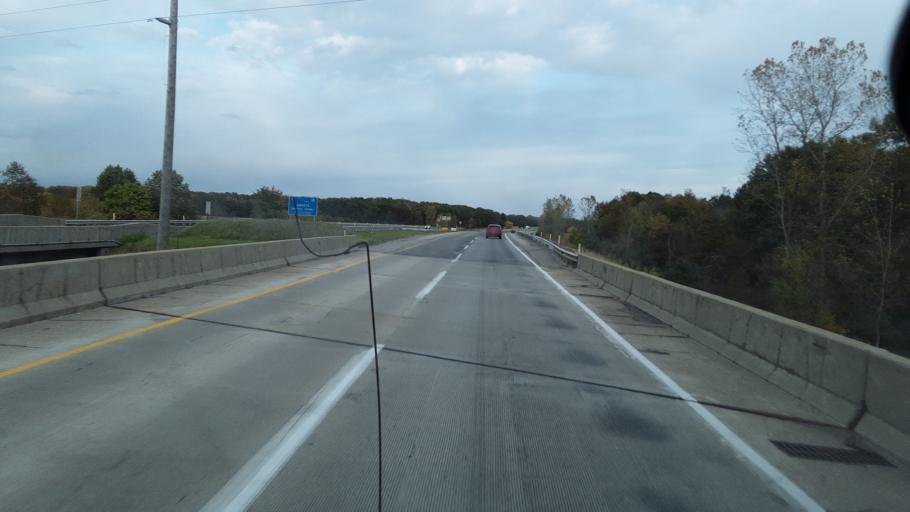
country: US
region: Indiana
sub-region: Elkhart County
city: Middlebury
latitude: 41.7426
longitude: -85.7288
